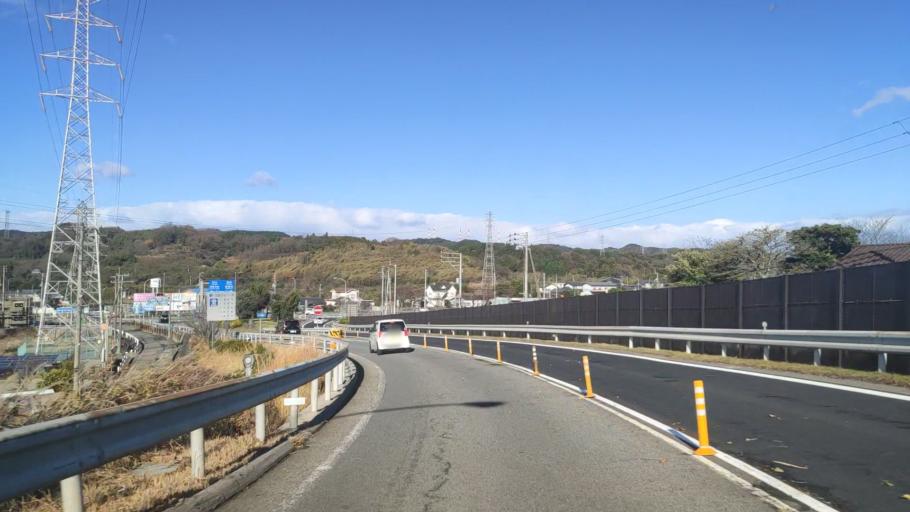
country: JP
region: Ehime
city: Saijo
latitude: 33.9179
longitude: 133.2403
